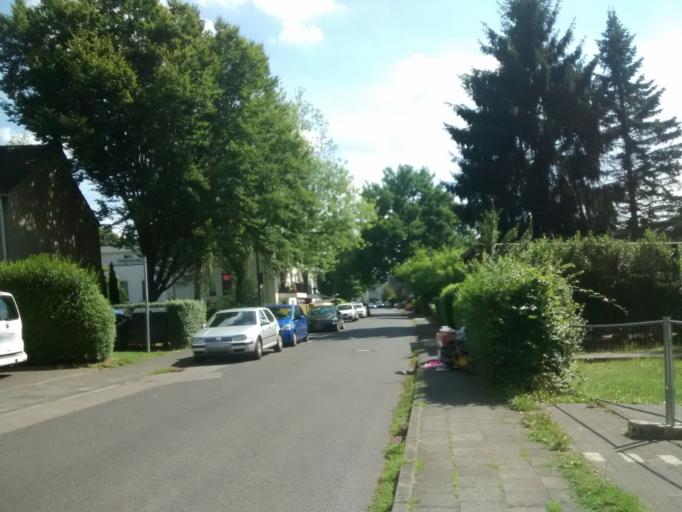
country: DE
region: North Rhine-Westphalia
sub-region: Regierungsbezirk Koln
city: Buchheim
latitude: 50.9872
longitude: 7.0396
